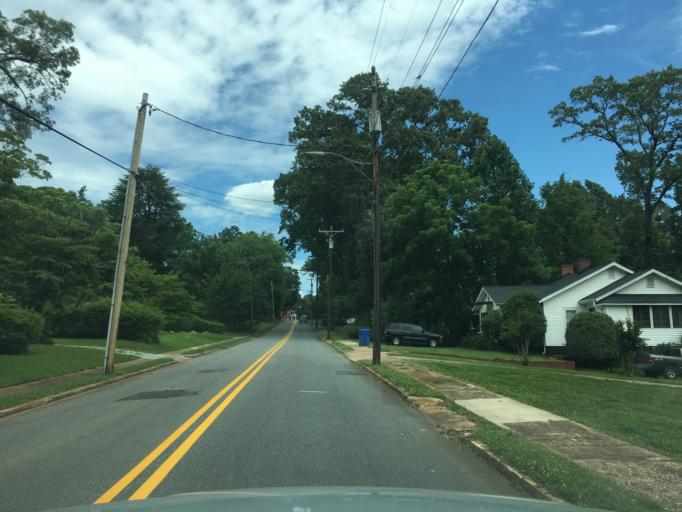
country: US
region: North Carolina
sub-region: Rutherford County
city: Rutherfordton
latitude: 35.3662
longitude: -81.9654
